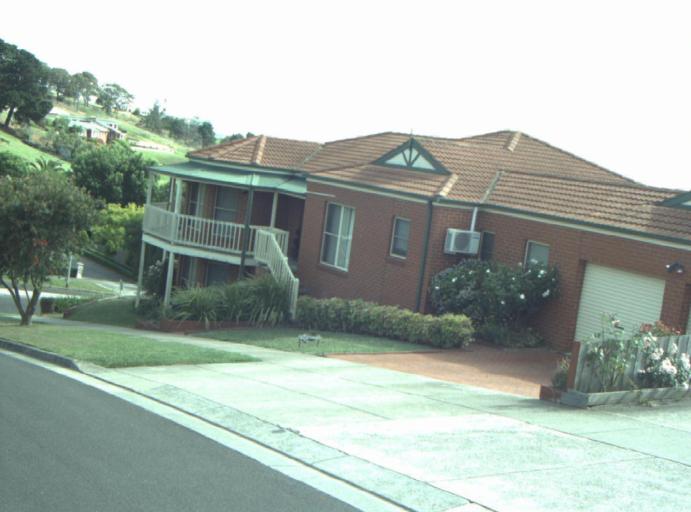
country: AU
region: Victoria
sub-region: Greater Geelong
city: Wandana Heights
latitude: -38.1601
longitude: 144.3154
